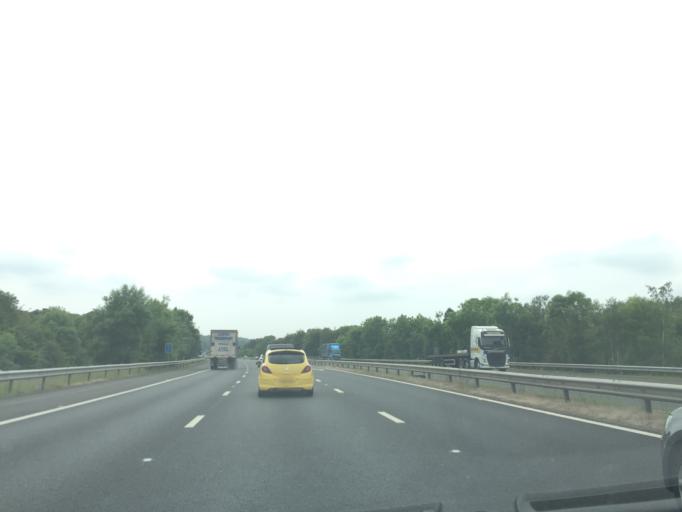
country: GB
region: England
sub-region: Hampshire
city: Cadnam
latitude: 50.9221
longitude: -1.5866
